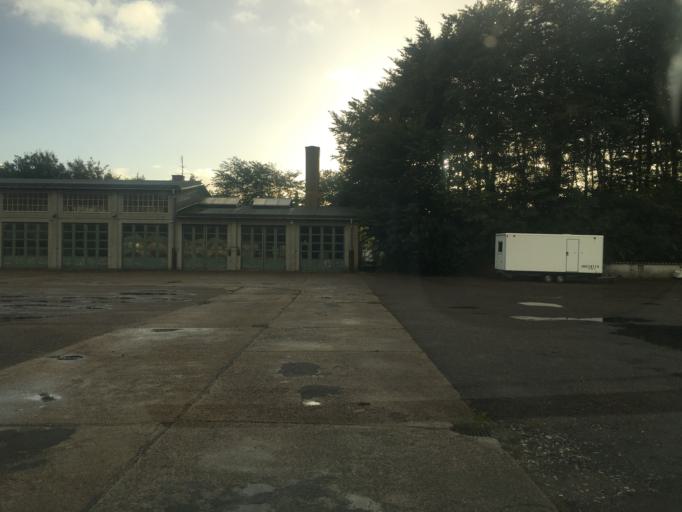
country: DK
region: South Denmark
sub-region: Tonder Kommune
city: Tonder
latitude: 54.9512
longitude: 8.8768
